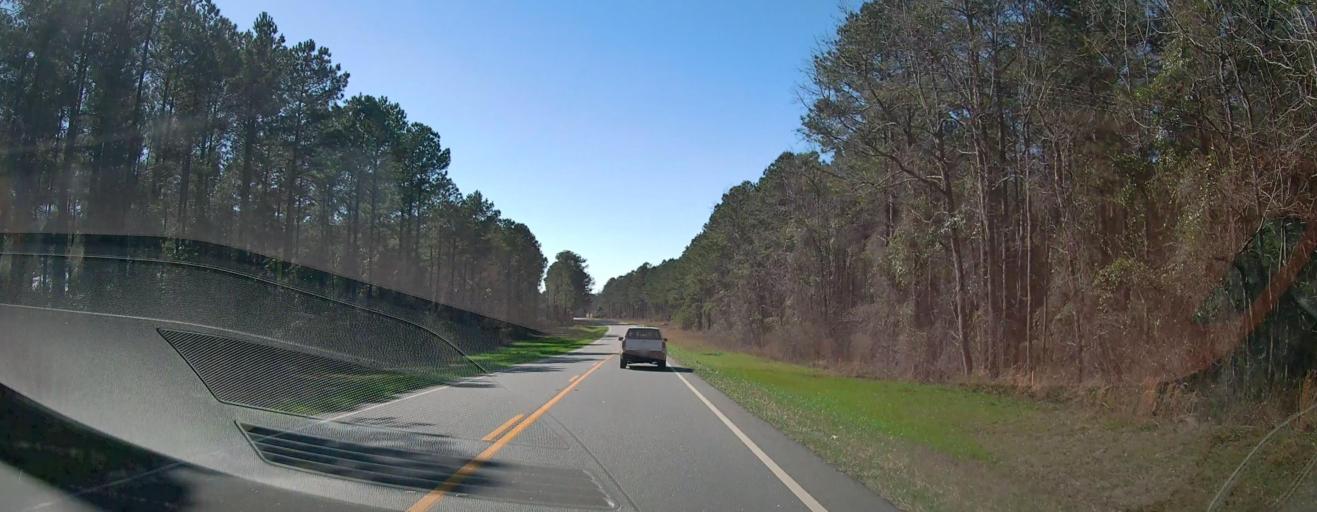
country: US
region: Georgia
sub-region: Dooly County
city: Unadilla
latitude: 32.3380
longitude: -83.8477
